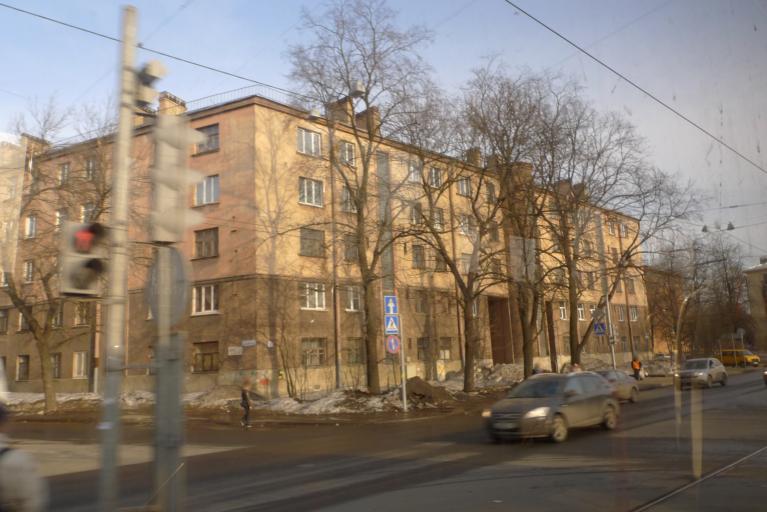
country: RU
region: Leningrad
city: Sampsonievskiy
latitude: 59.9820
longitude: 30.3433
